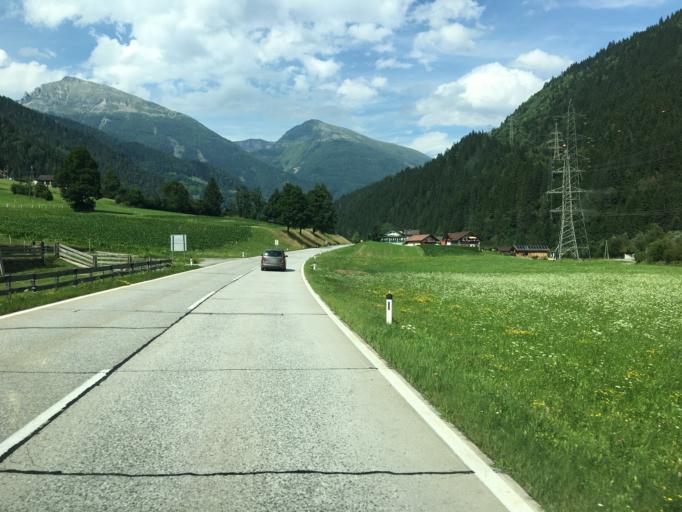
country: AT
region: Carinthia
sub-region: Politischer Bezirk Spittal an der Drau
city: Stall
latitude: 46.9154
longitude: 13.0705
